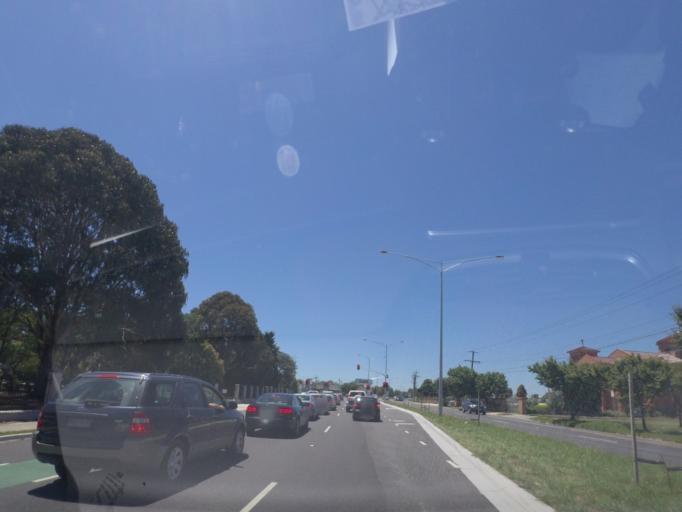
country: AU
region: Victoria
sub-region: Whittlesea
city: Lalor
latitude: -37.6581
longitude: 145.0197
